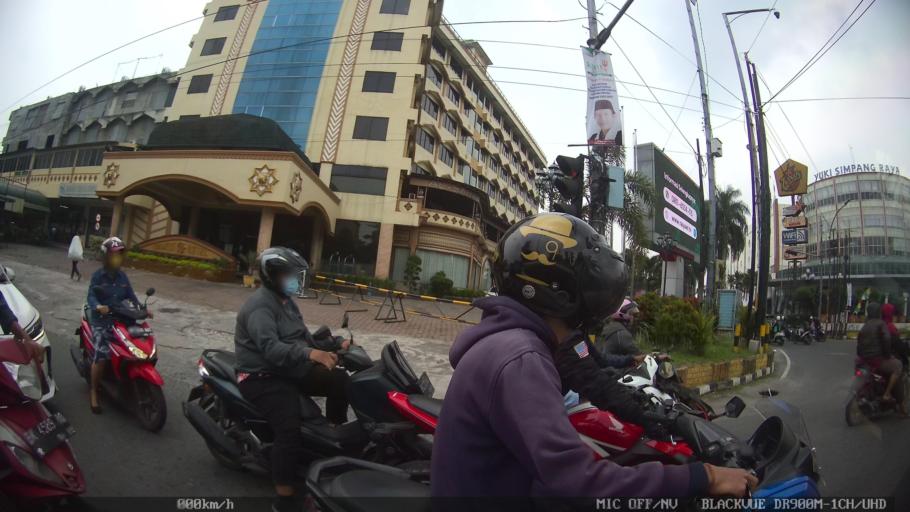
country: ID
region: North Sumatra
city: Medan
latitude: 3.5763
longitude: 98.6877
